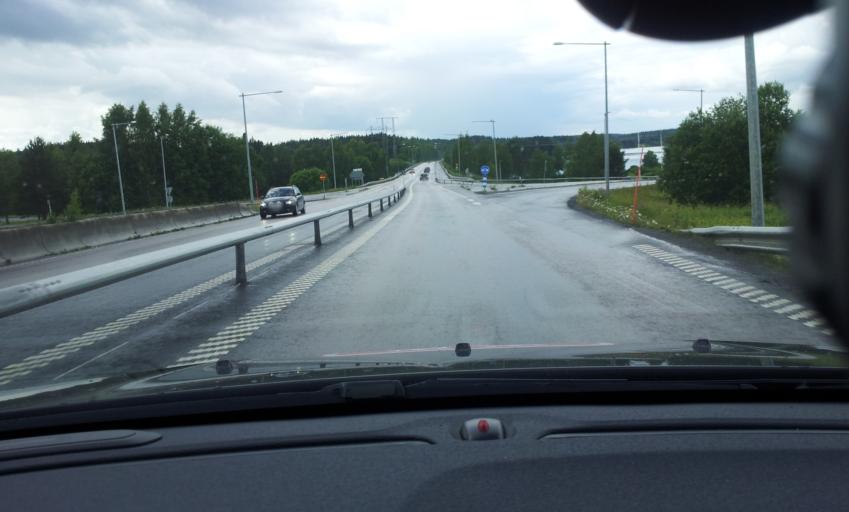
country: SE
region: Jaemtland
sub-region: Krokoms Kommun
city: Krokom
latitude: 63.3146
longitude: 14.4608
